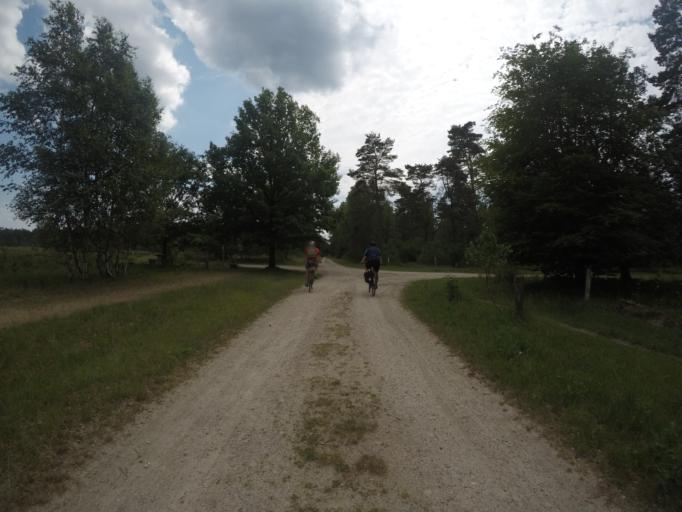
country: DE
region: Lower Saxony
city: Asendorf
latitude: 53.2473
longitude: 9.9571
